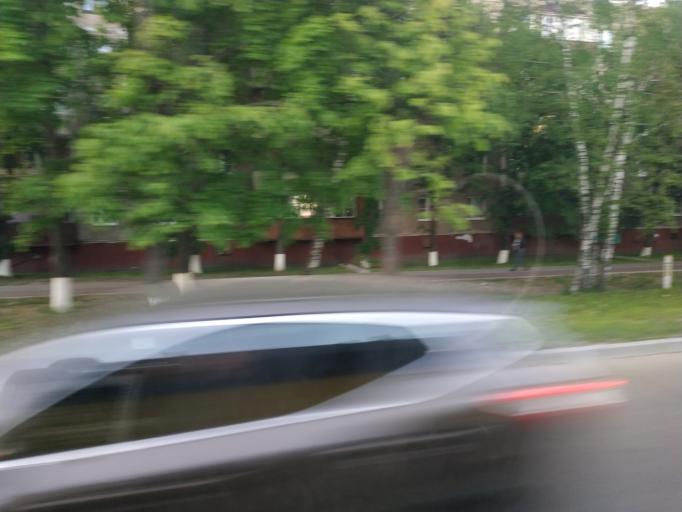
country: RU
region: Moskovskaya
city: Domodedovo
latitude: 55.4437
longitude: 37.7447
